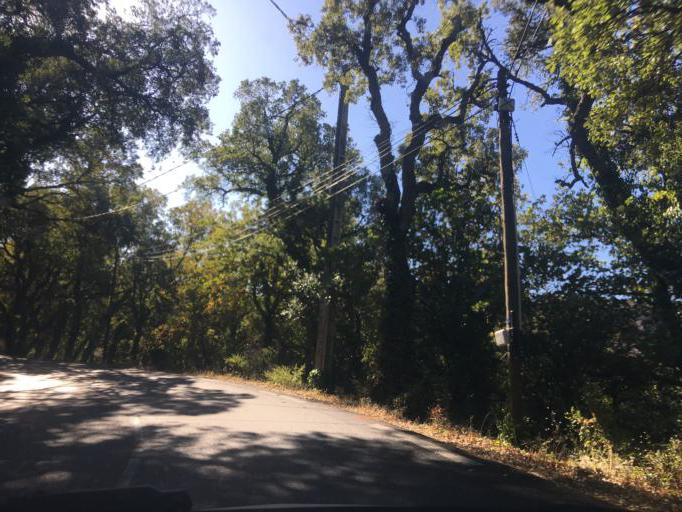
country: FR
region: Provence-Alpes-Cote d'Azur
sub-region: Departement du Var
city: La Garde-Freinet
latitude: 43.3248
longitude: 6.4741
